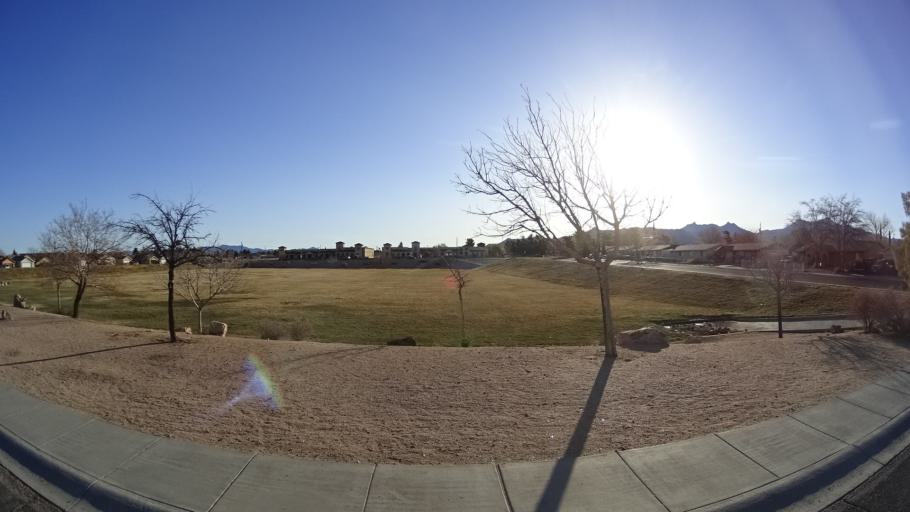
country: US
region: Arizona
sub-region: Mohave County
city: Kingman
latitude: 35.1961
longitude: -114.0137
